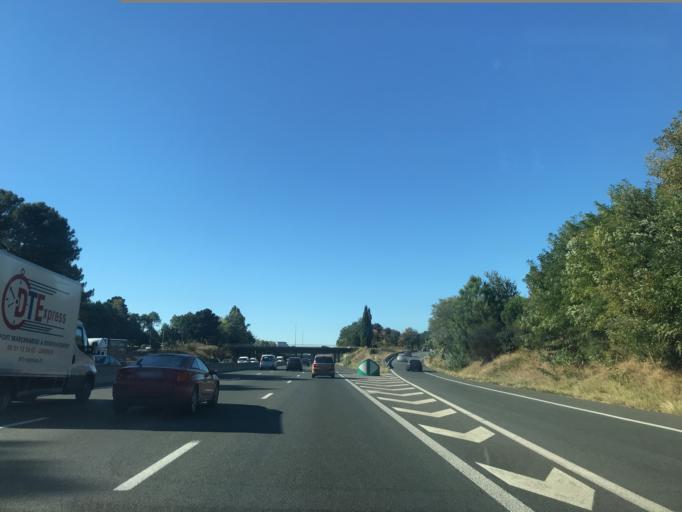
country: FR
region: Aquitaine
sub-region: Departement de la Gironde
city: Pessac
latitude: 44.8025
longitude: -0.6592
